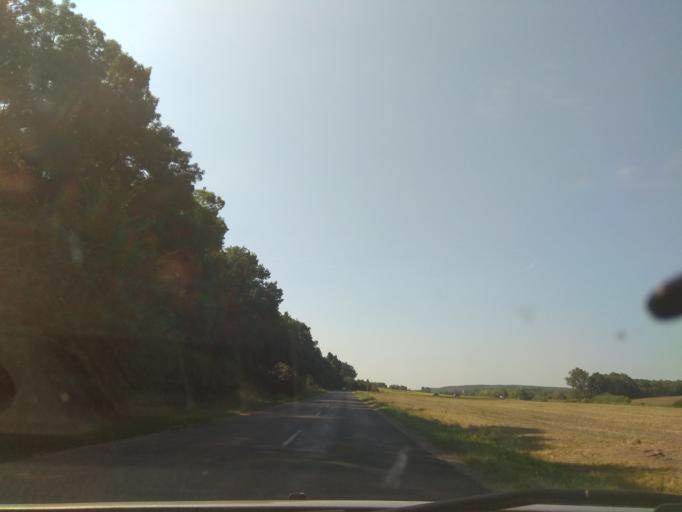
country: HU
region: Borsod-Abauj-Zemplen
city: Harsany
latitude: 47.9430
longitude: 20.7437
